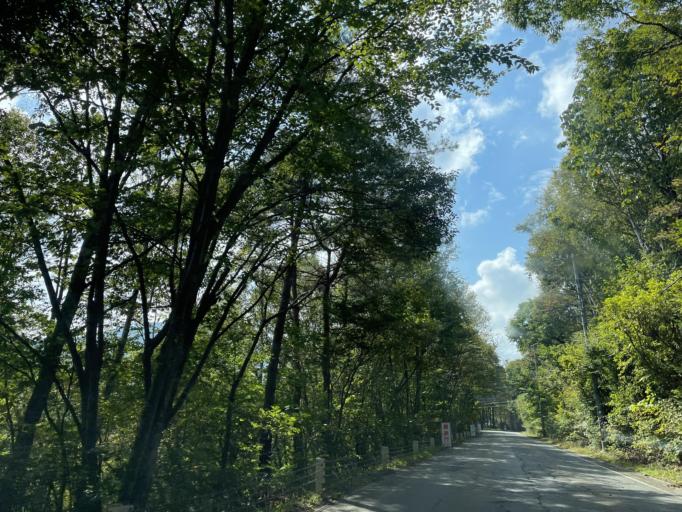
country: JP
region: Nagano
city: Omachi
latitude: 36.5179
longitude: 137.7805
